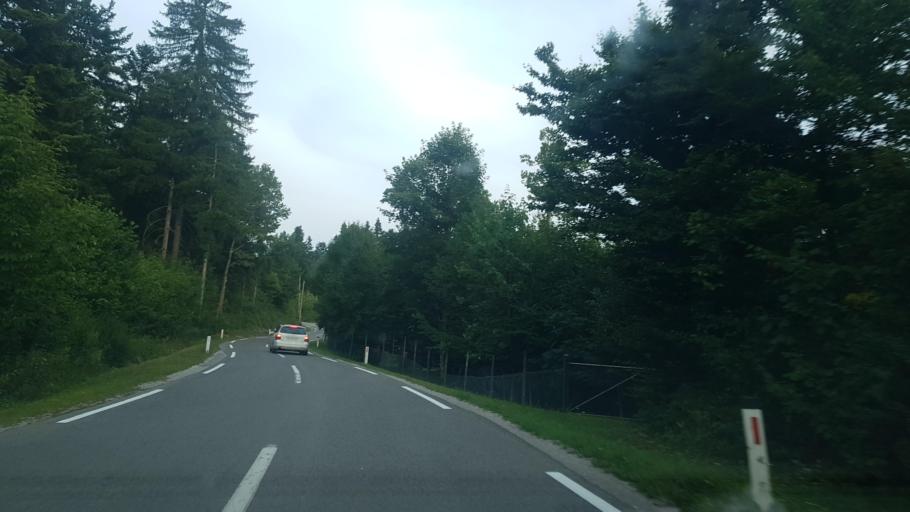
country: SI
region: Logatec
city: Logatec
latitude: 45.8950
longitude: 14.1799
